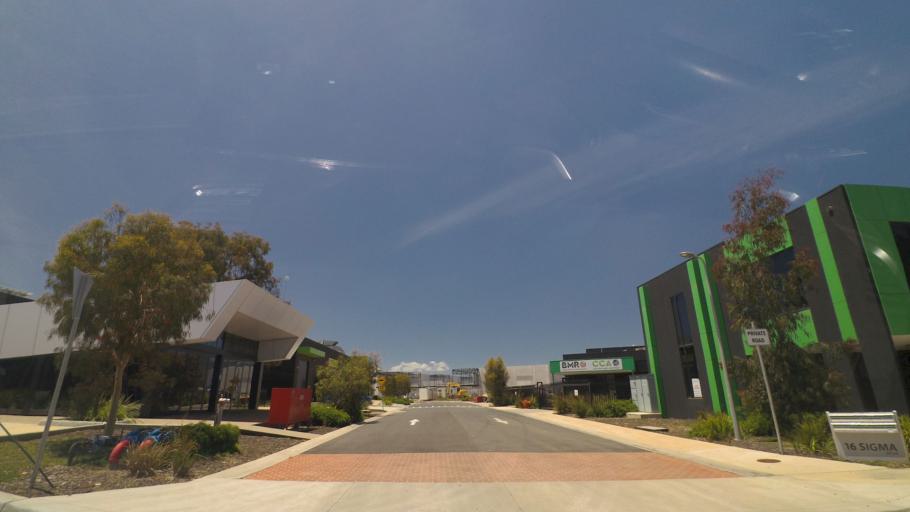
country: AU
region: Victoria
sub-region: Maroondah
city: Bayswater North
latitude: -37.8163
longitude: 145.2951
